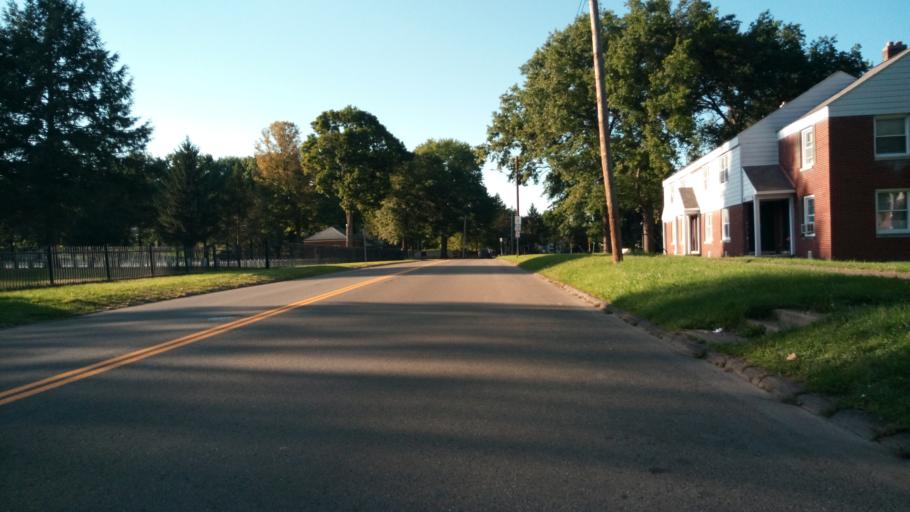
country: US
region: New York
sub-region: Chemung County
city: Elmira Heights
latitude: 42.1096
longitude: -76.8258
